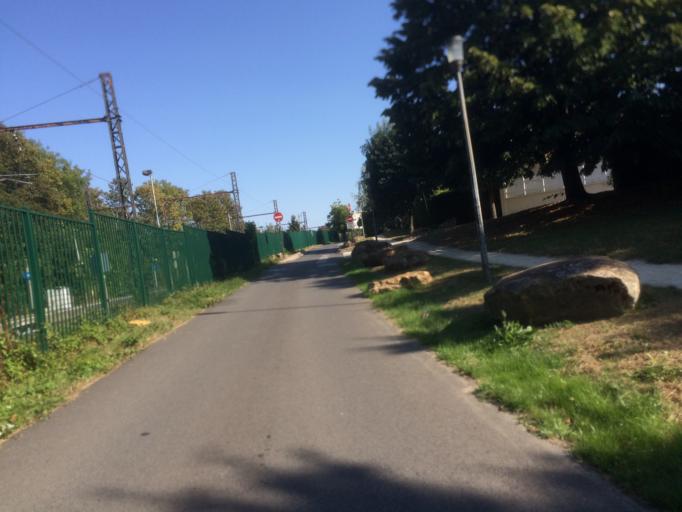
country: FR
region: Ile-de-France
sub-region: Departement de l'Essonne
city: Villemoisson-sur-Orge
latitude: 48.6767
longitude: 2.3321
